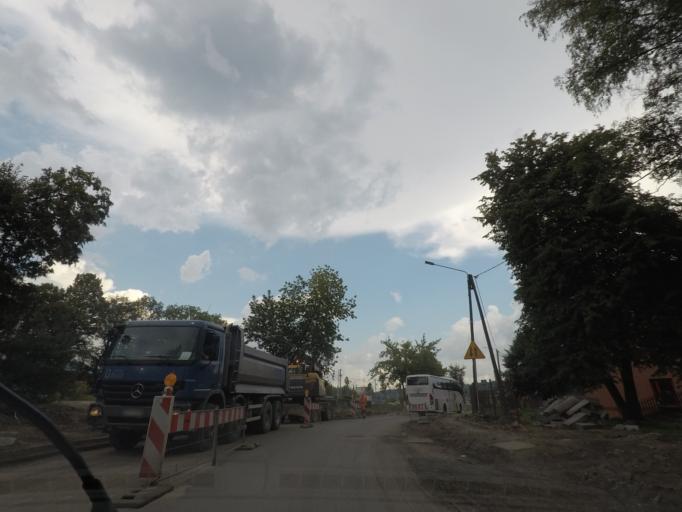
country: PL
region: Lesser Poland Voivodeship
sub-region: Powiat wielicki
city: Wieliczka
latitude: 49.9916
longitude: 20.0466
